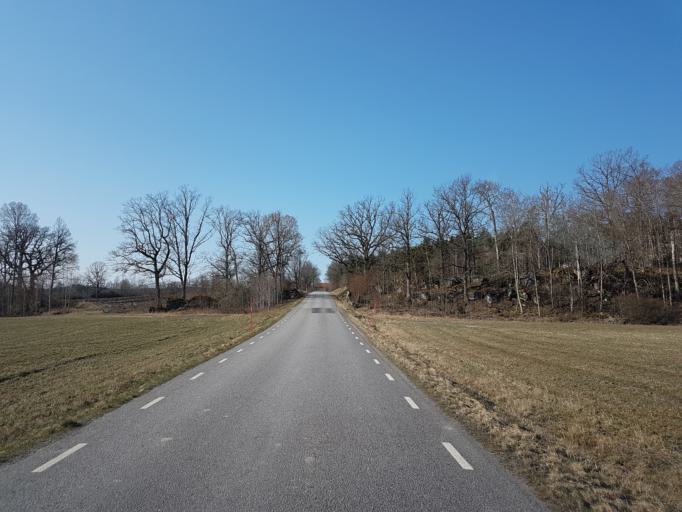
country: SE
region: OEstergoetland
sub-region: Valdemarsviks Kommun
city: Gusum
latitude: 58.1986
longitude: 16.3425
